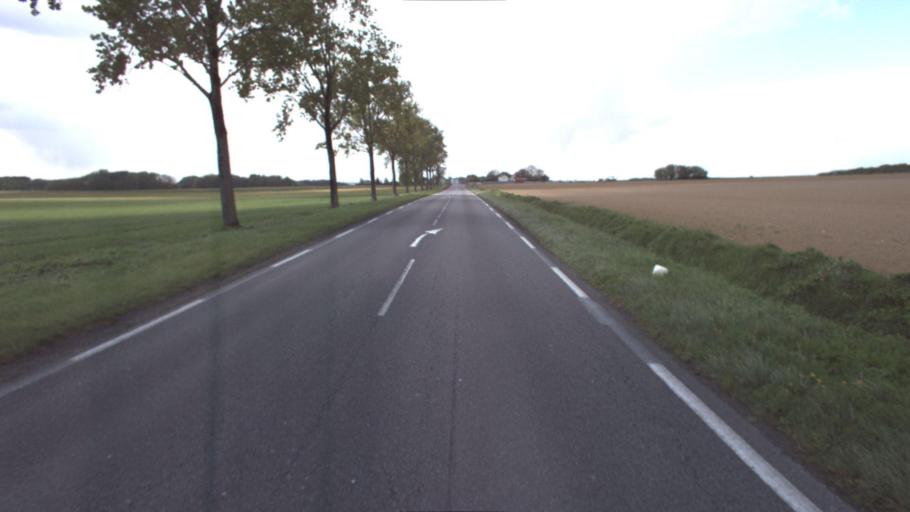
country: FR
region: Ile-de-France
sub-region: Departement de Seine-et-Marne
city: Jouy-le-Chatel
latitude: 48.6926
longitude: 3.1908
